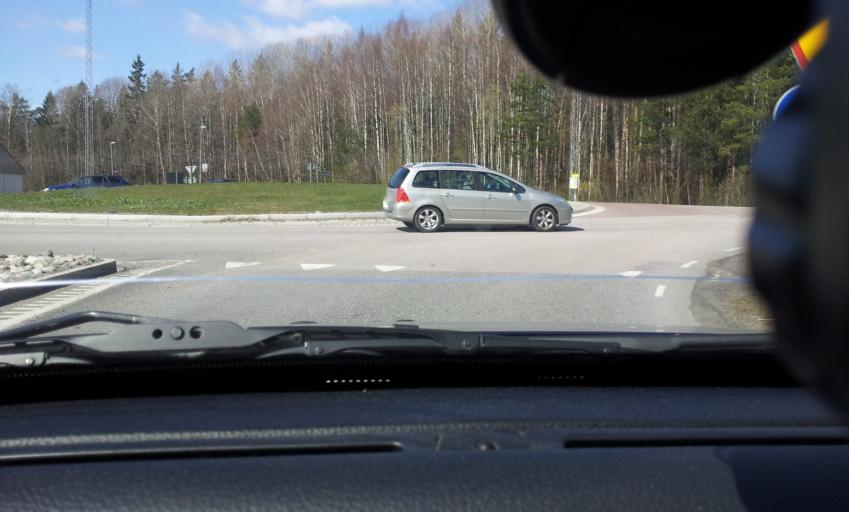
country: SE
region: Stockholm
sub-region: Haninge Kommun
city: Haninge
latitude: 59.1909
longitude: 18.1781
